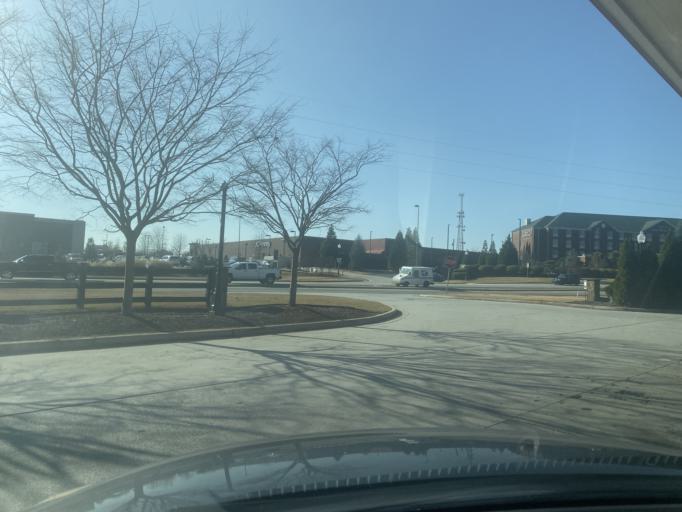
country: US
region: Georgia
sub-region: Henry County
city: McDonough
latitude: 33.4250
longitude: -84.1842
